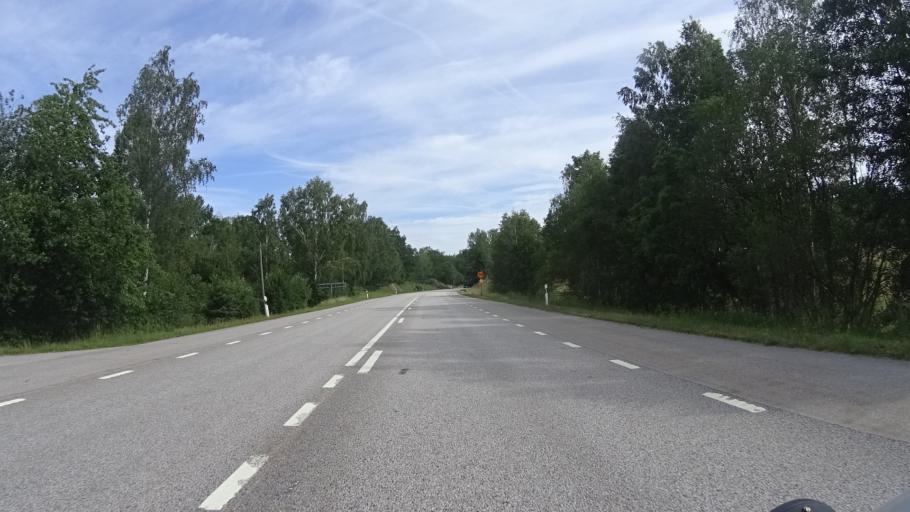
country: SE
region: Kalmar
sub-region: Vasterviks Kommun
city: Ankarsrum
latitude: 57.7156
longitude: 16.4503
